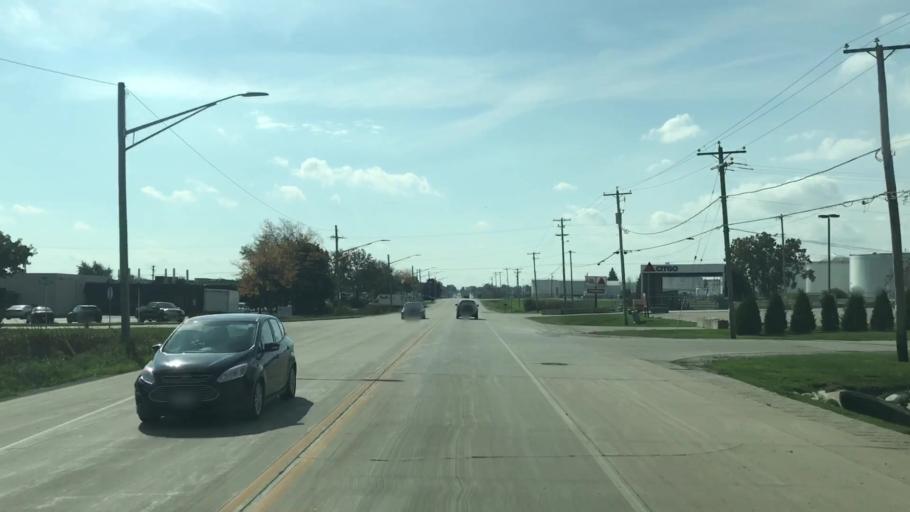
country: US
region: Wisconsin
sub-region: Waukesha County
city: Menomonee Falls
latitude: 43.1871
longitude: -88.0440
